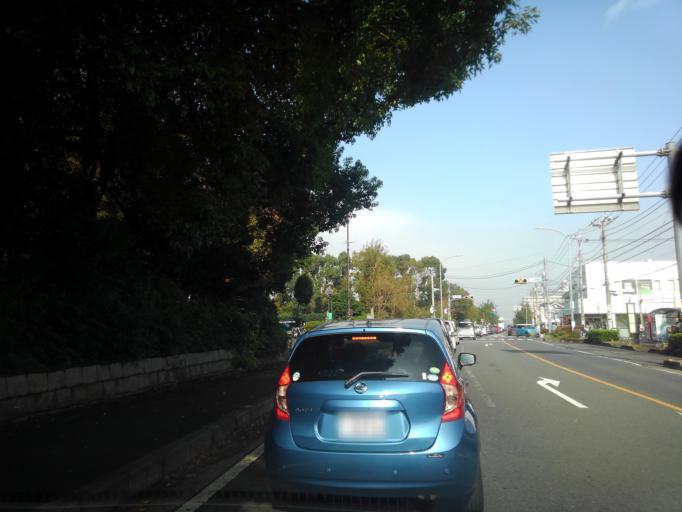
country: JP
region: Saitama
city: Tokorozawa
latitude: 35.7985
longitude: 139.4799
